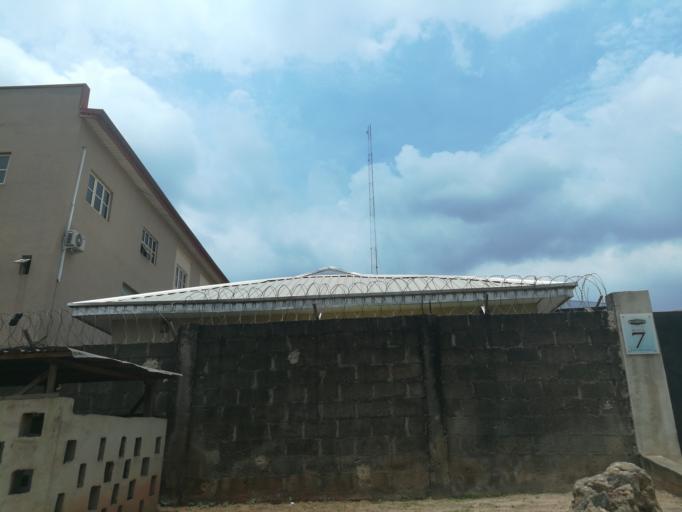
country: NG
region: Lagos
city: Ojota
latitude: 6.5933
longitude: 3.3684
